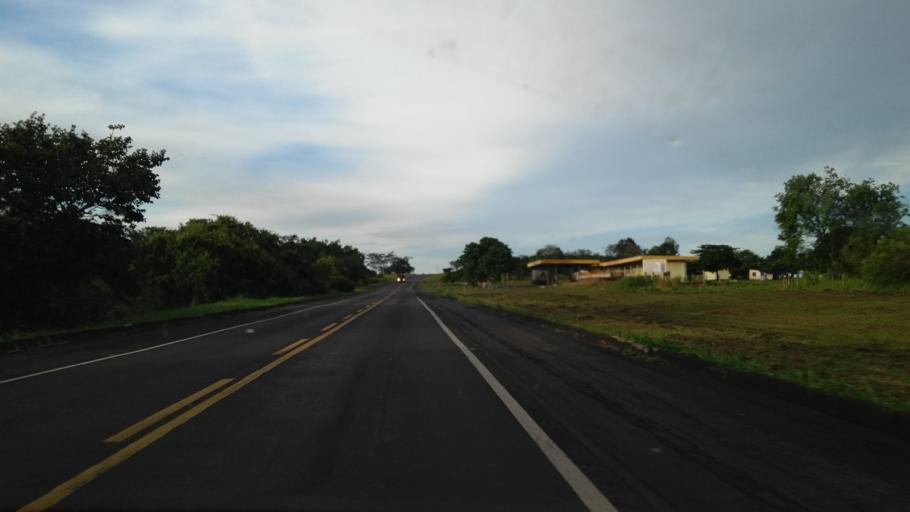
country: BR
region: Sao Paulo
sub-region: Marilia
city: Marilia
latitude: -21.9219
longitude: -49.9168
